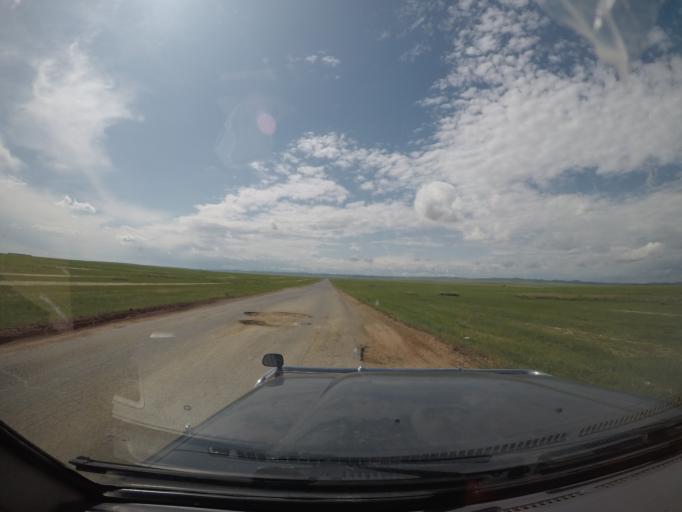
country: MN
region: Hentiy
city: Moron
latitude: 47.4210
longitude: 110.0554
